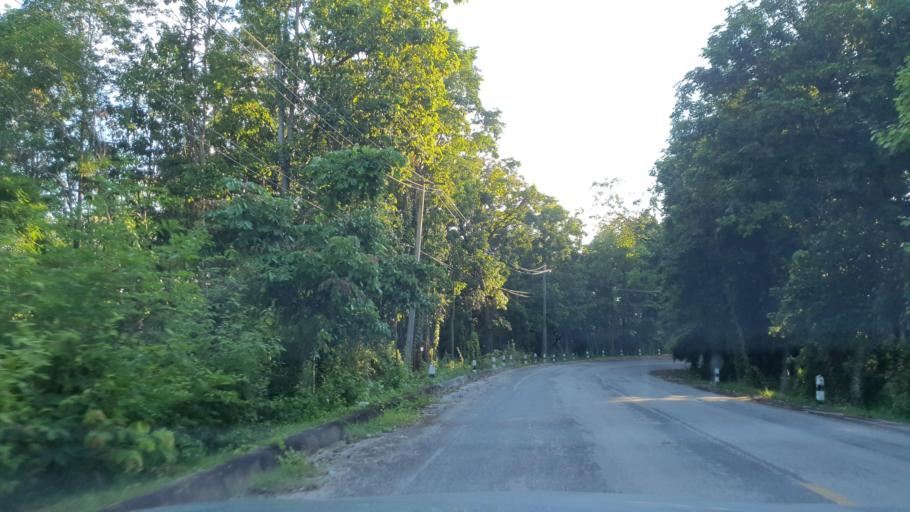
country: TH
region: Chiang Mai
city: Mae On
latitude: 18.8245
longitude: 99.2967
